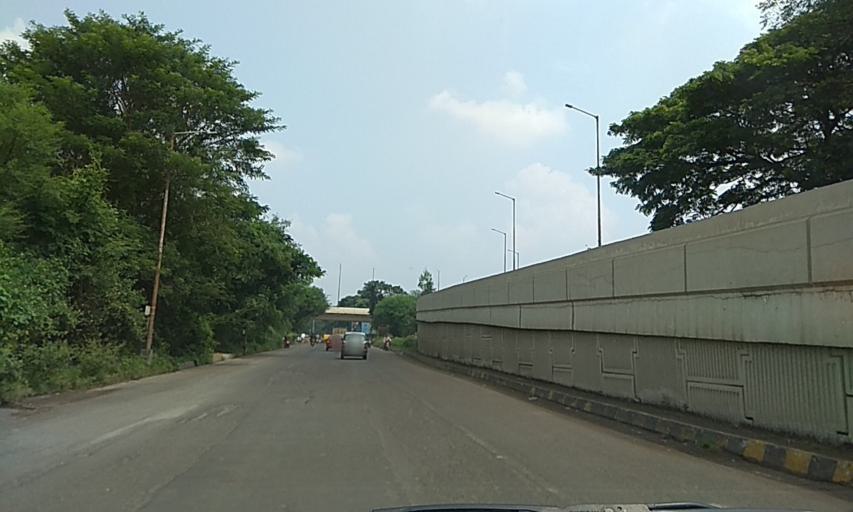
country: IN
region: Maharashtra
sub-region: Pune Division
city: Khadki
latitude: 18.5548
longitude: 73.8602
